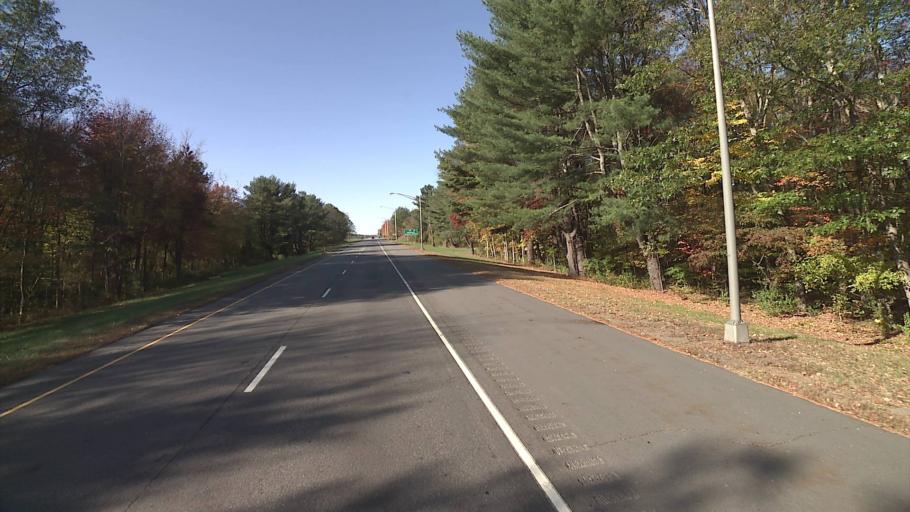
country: US
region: Connecticut
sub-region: Windham County
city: Willimantic
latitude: 41.7294
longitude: -72.2324
